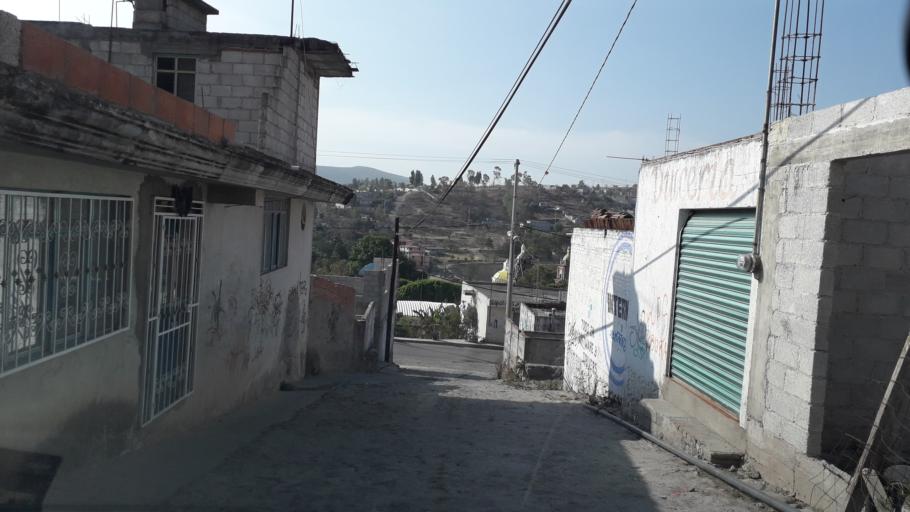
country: MX
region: Puebla
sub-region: Puebla
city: San Andres Azumiatla
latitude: 18.9039
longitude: -98.2527
